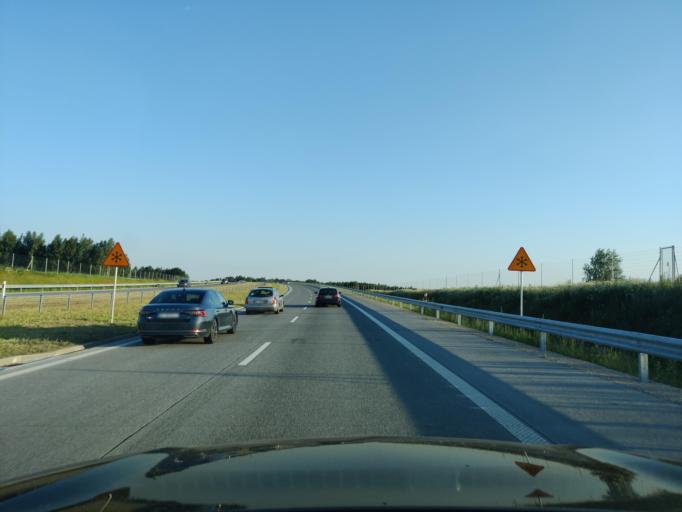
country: PL
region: Masovian Voivodeship
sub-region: Powiat mlawski
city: Wisniewo
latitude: 53.0149
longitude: 20.3373
